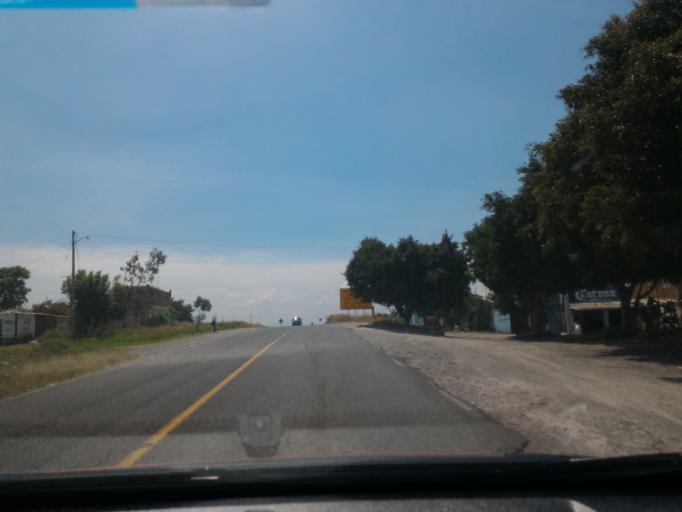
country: MX
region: Guanajuato
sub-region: Penjamo
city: Estacion la Piedad
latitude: 20.4106
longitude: -101.9974
